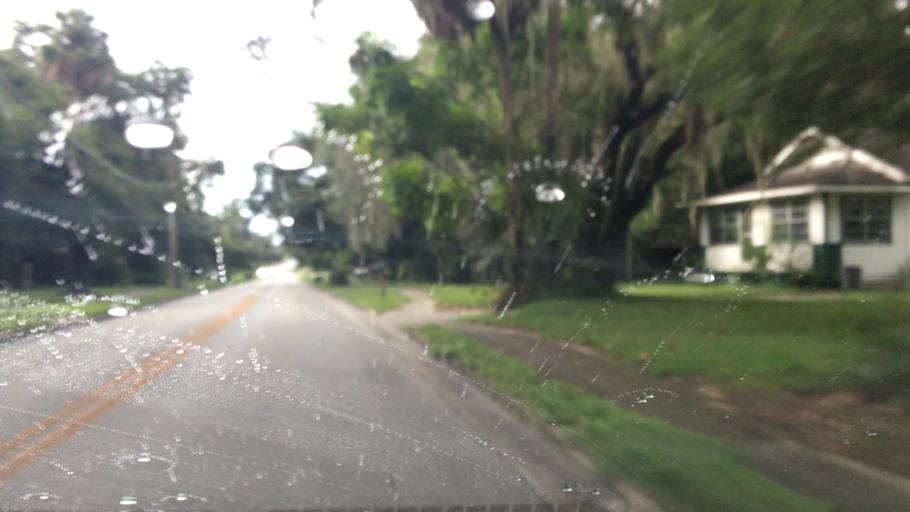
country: US
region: Florida
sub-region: Seminole County
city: Sanford
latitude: 28.7952
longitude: -81.2560
